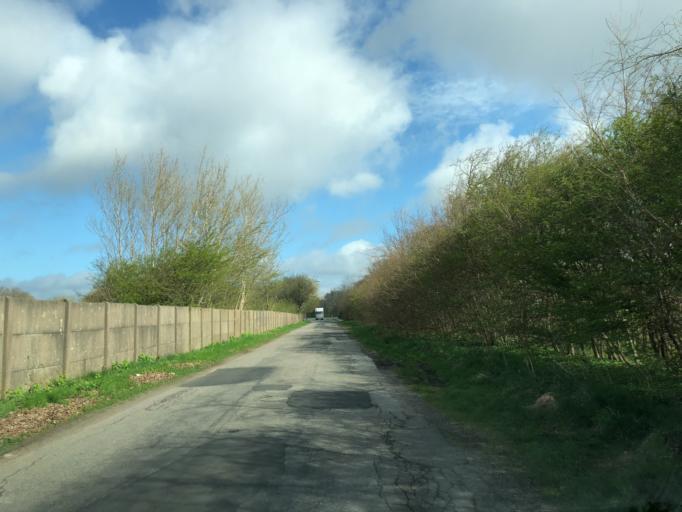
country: DK
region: North Denmark
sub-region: Alborg Kommune
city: Aalborg
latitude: 57.0523
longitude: 9.8835
